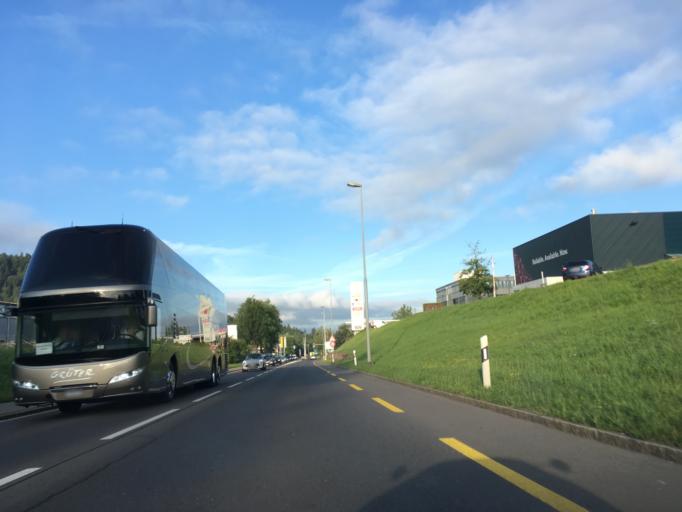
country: CH
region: Zug
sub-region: Zug
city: Baar
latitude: 47.2140
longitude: 8.5654
